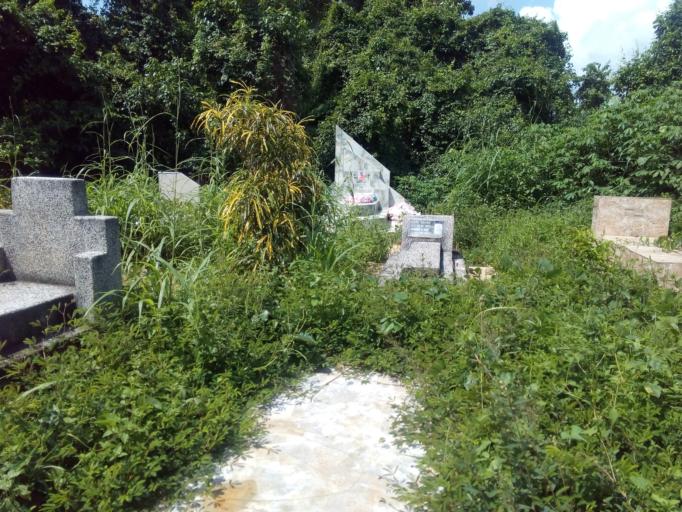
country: CI
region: Sud-Comoe
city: Mafere
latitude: 5.2962
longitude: -2.7862
